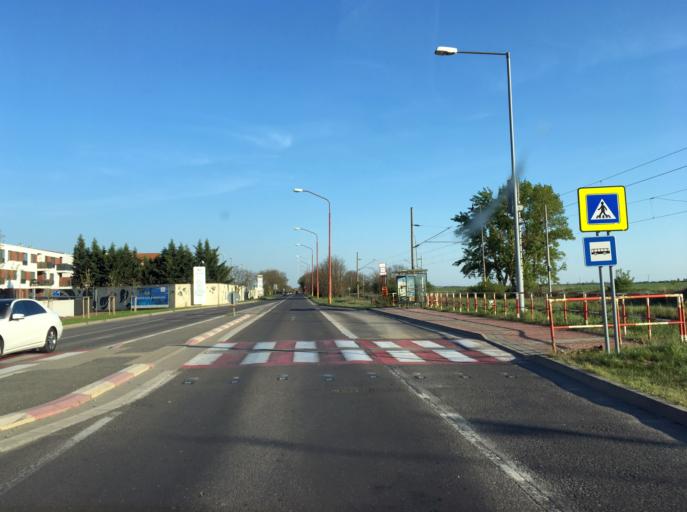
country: AT
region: Burgenland
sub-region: Politischer Bezirk Neusiedl am See
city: Deutsch Jahrndorf
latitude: 48.0430
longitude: 17.1560
